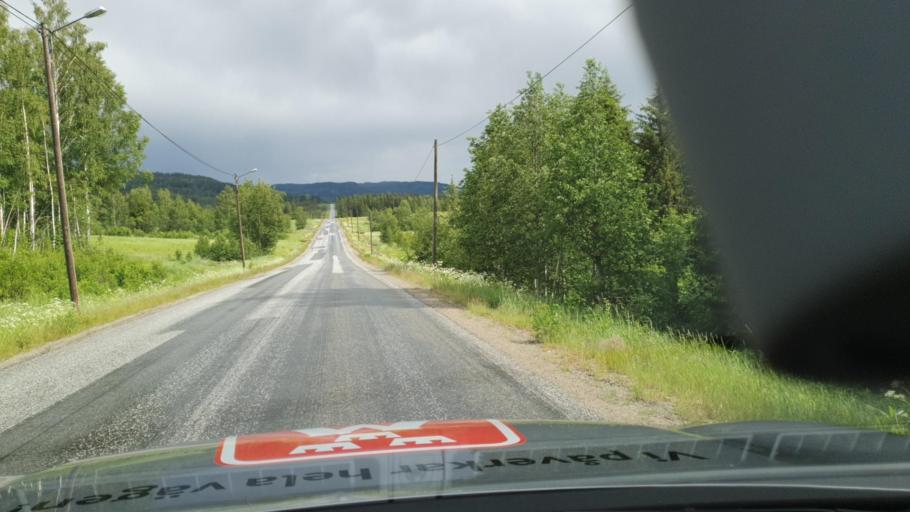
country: SE
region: Vaesternorrland
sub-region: OErnskoeldsviks Kommun
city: Bredbyn
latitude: 63.3738
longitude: 17.9359
